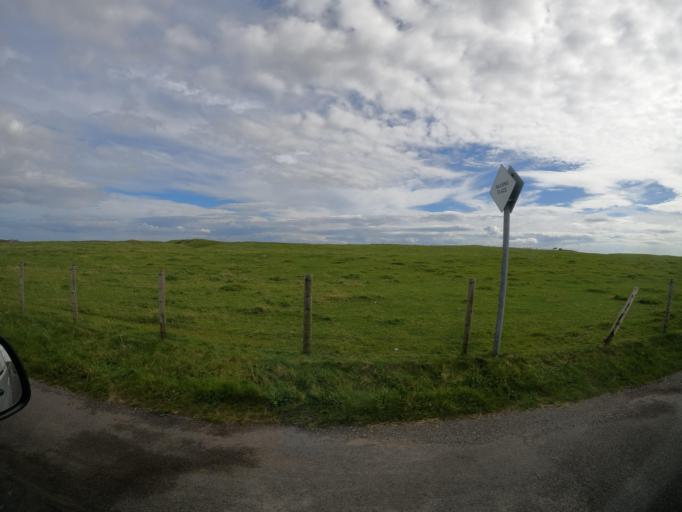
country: GB
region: Scotland
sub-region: Eilean Siar
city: Barra
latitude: 56.4822
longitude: -6.9008
